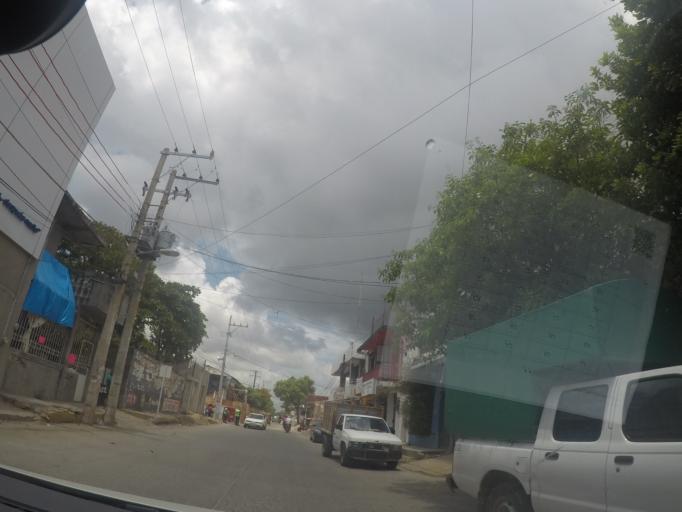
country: MX
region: Oaxaca
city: Juchitan de Zaragoza
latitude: 16.4330
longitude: -95.0238
